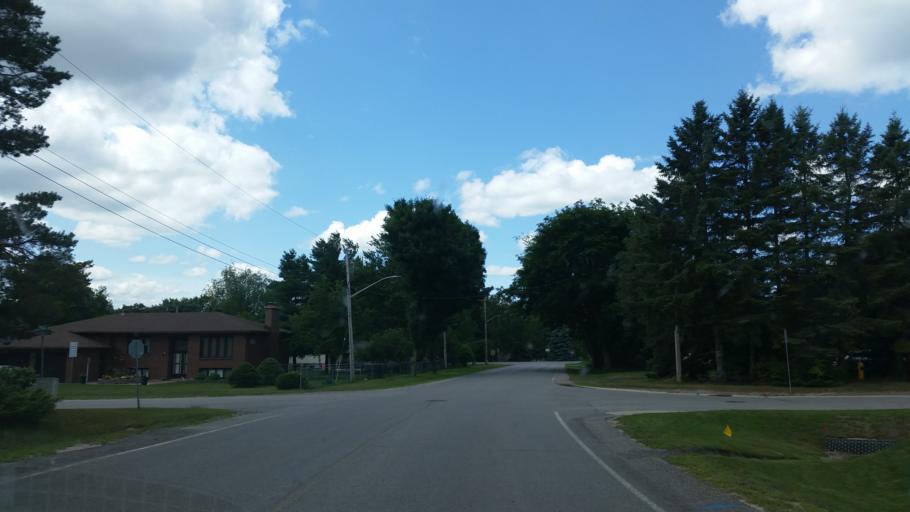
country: CA
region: Ontario
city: Barrie
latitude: 44.4459
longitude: -79.7203
